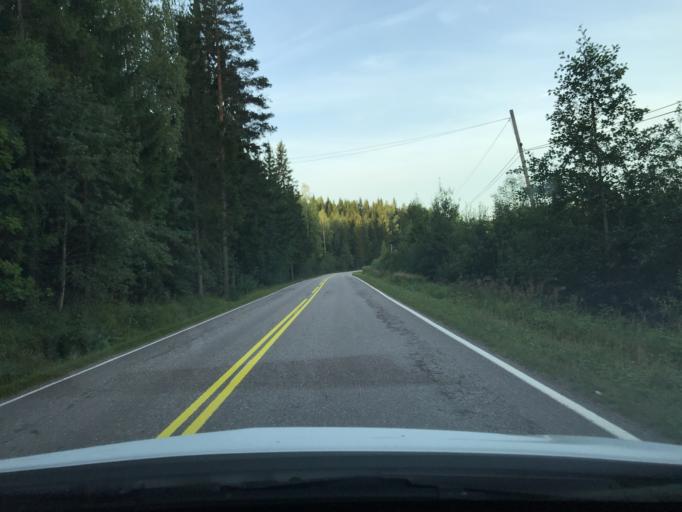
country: FI
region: Uusimaa
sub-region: Helsinki
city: Vihti
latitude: 60.4215
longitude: 24.5069
